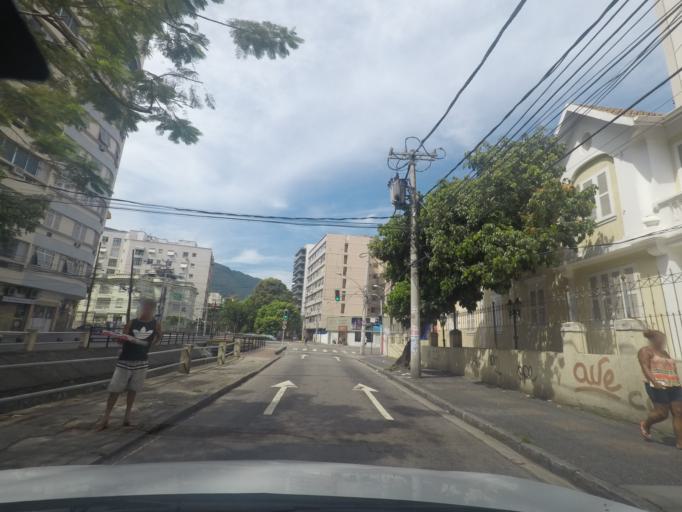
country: BR
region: Rio de Janeiro
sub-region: Rio De Janeiro
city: Rio de Janeiro
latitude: -22.9304
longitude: -43.2419
